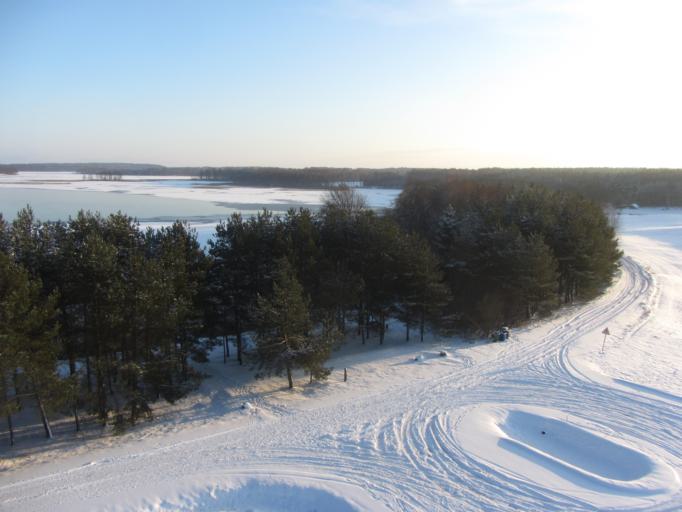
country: LT
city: Veisiejai
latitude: 54.1011
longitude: 23.7219
